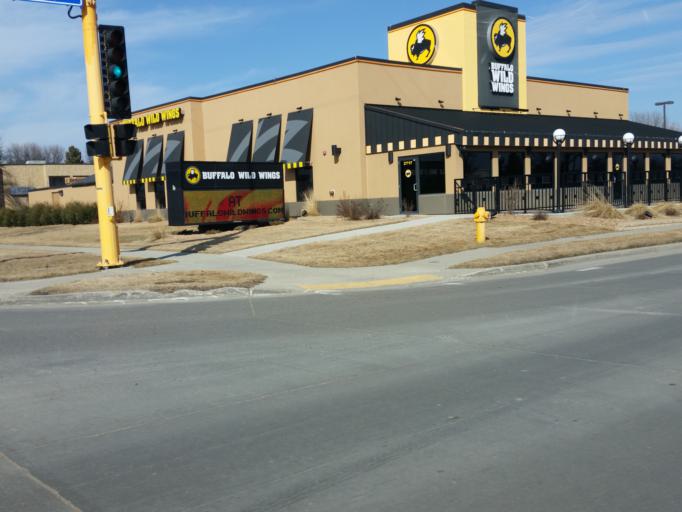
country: US
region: North Dakota
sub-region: Grand Forks County
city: Grand Forks
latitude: 47.8922
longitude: -97.0666
